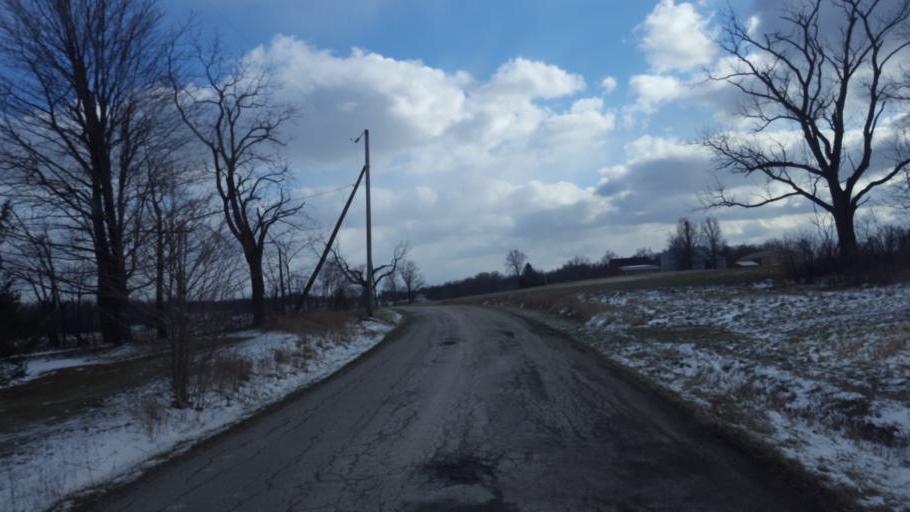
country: US
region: Ohio
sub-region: Crawford County
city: Galion
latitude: 40.7043
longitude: -82.7177
